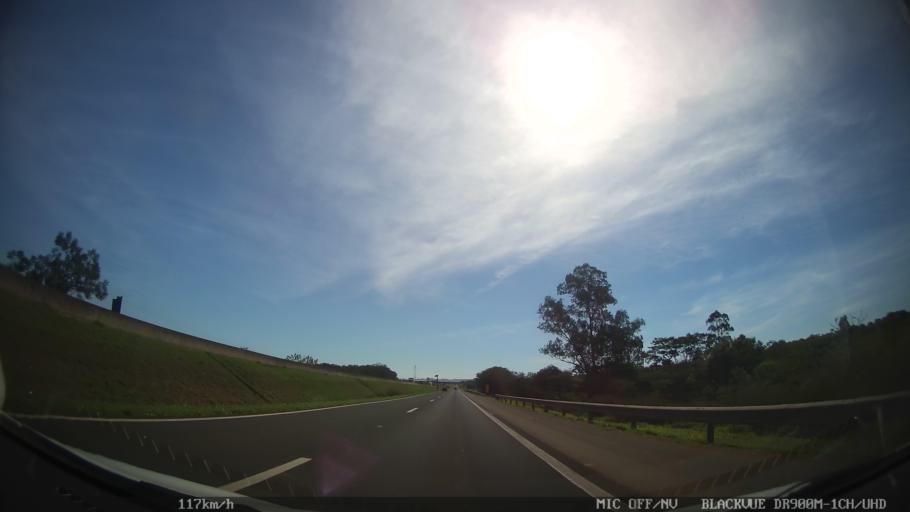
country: BR
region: Sao Paulo
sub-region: Porto Ferreira
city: Porto Ferreira
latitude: -21.8402
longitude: -47.4951
